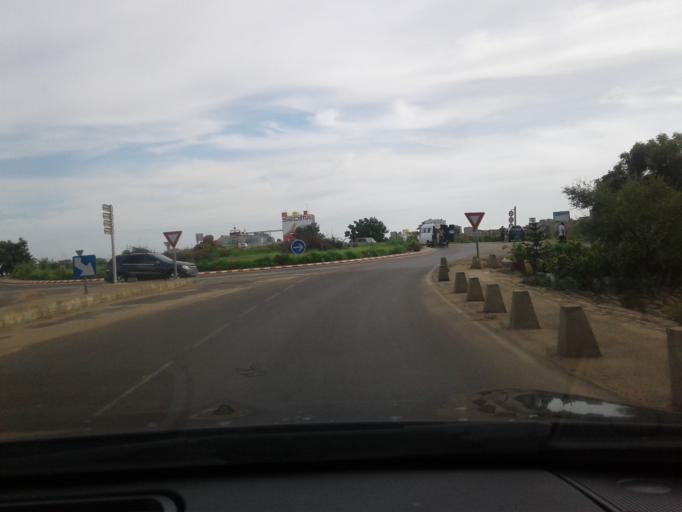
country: SN
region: Dakar
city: Pikine
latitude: 14.7448
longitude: -17.2886
